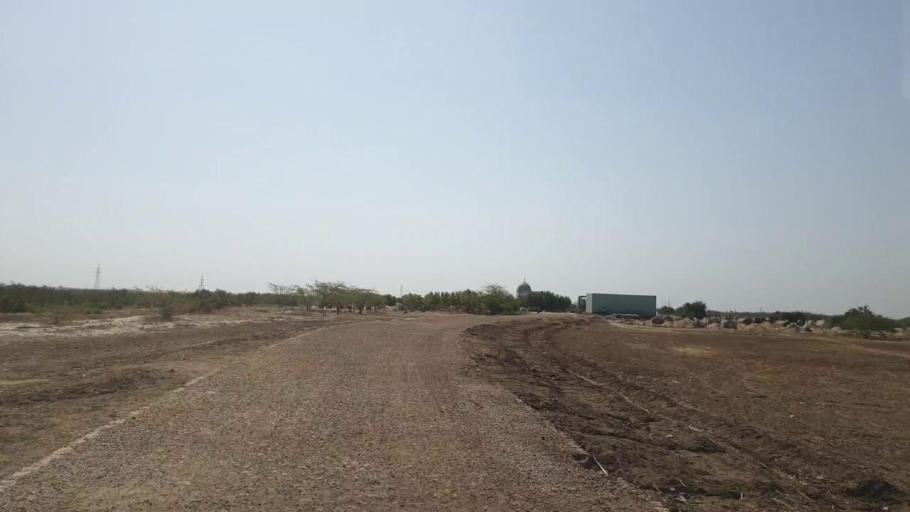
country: PK
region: Sindh
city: Naukot
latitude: 24.9713
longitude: 69.4696
